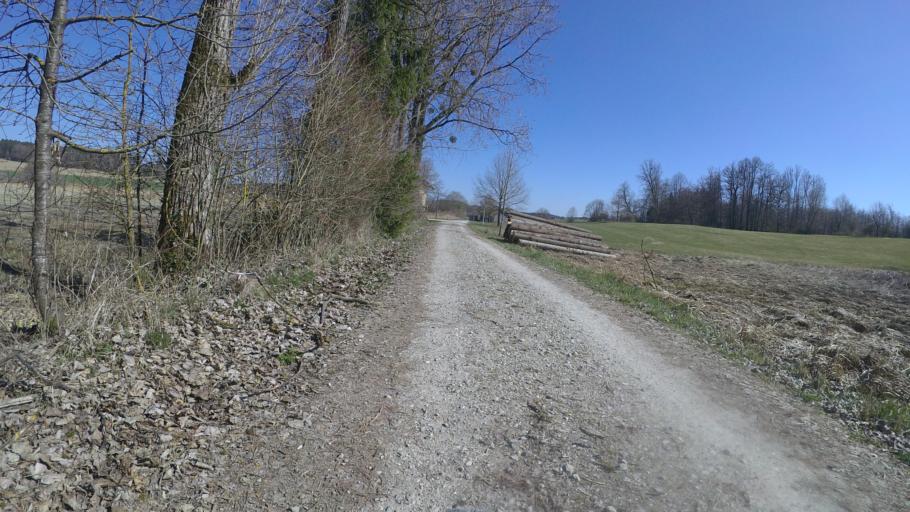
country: DE
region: Bavaria
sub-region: Upper Bavaria
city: Seeon-Seebruck
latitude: 47.9646
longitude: 12.4891
